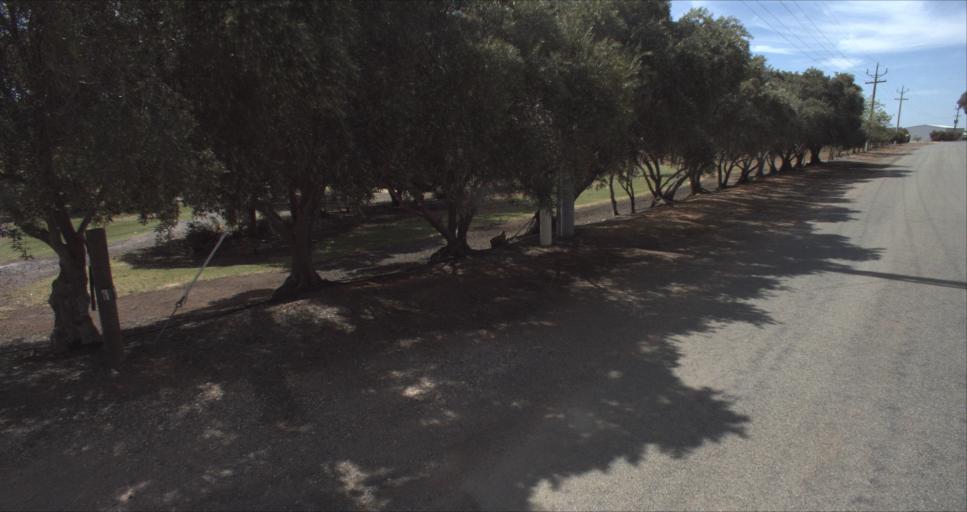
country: AU
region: New South Wales
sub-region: Leeton
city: Leeton
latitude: -34.5618
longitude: 146.4601
